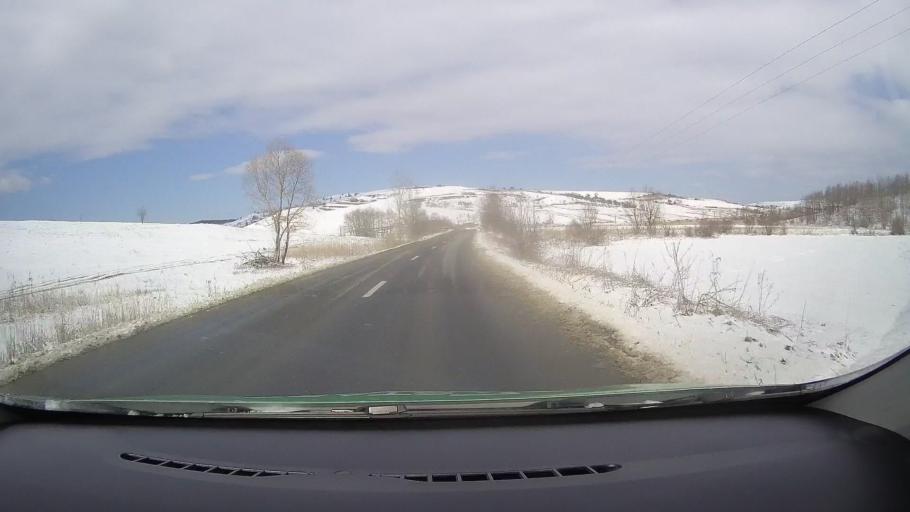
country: RO
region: Sibiu
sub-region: Comuna Altina
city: Altina
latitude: 45.9747
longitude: 24.4658
